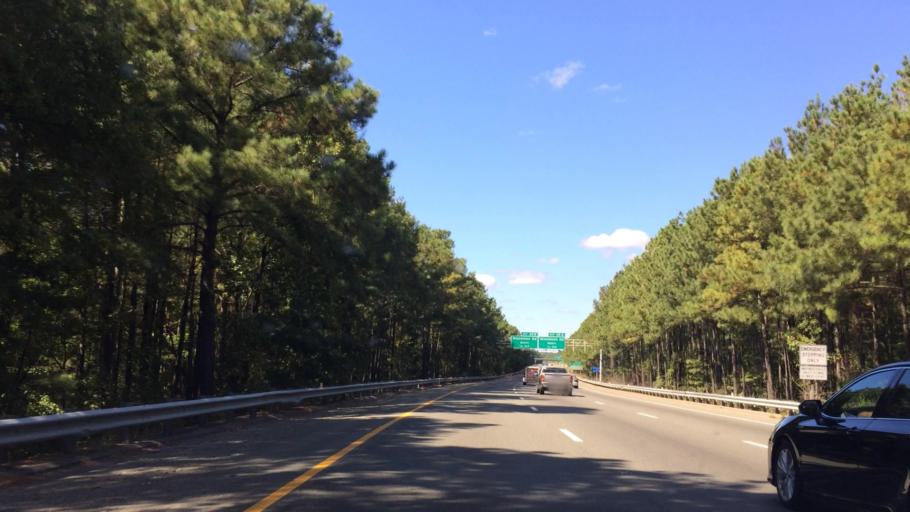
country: US
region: Virginia
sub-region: Henrico County
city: Glen Allen
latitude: 37.6618
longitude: -77.4748
